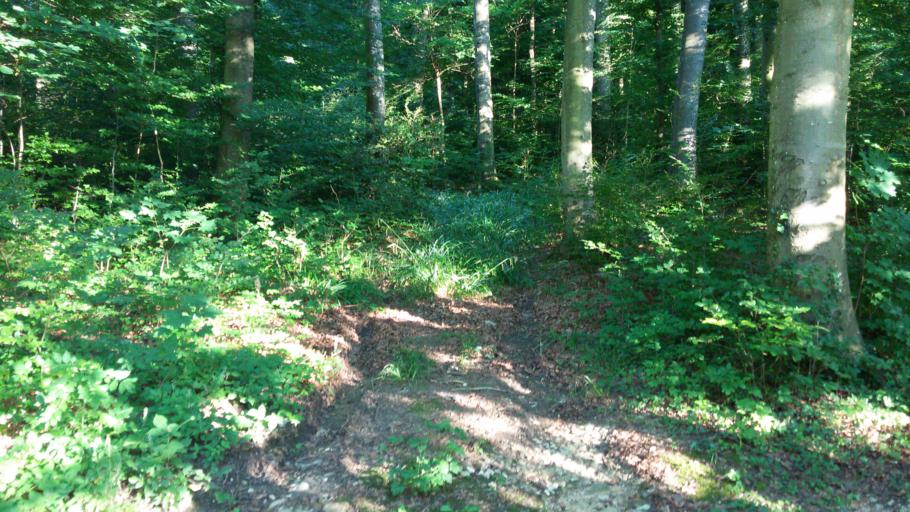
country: CH
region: Basel-Landschaft
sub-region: Bezirk Liestal
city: Pratteln
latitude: 47.5081
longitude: 7.6688
